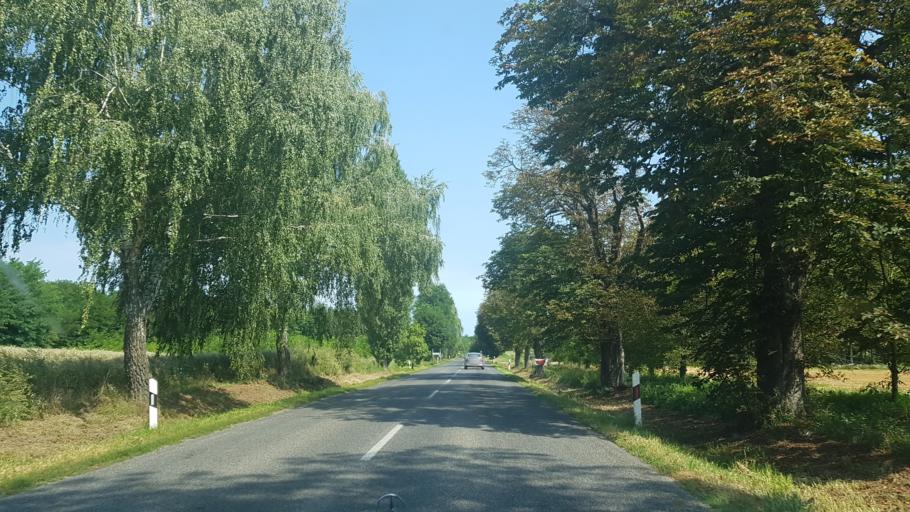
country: HU
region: Somogy
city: Marcali
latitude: 46.5125
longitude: 17.4244
